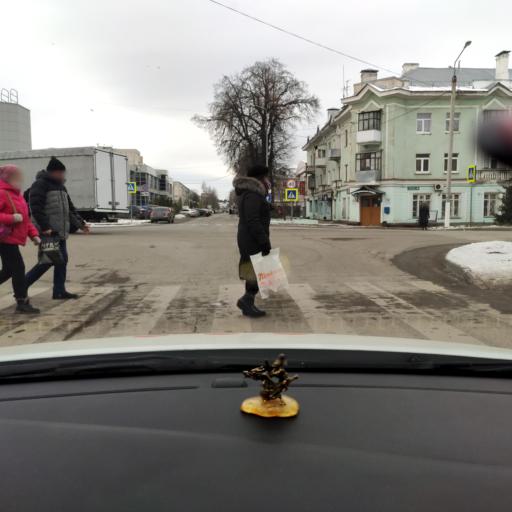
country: RU
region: Tatarstan
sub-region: Zelenodol'skiy Rayon
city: Zelenodolsk
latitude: 55.8508
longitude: 48.5023
